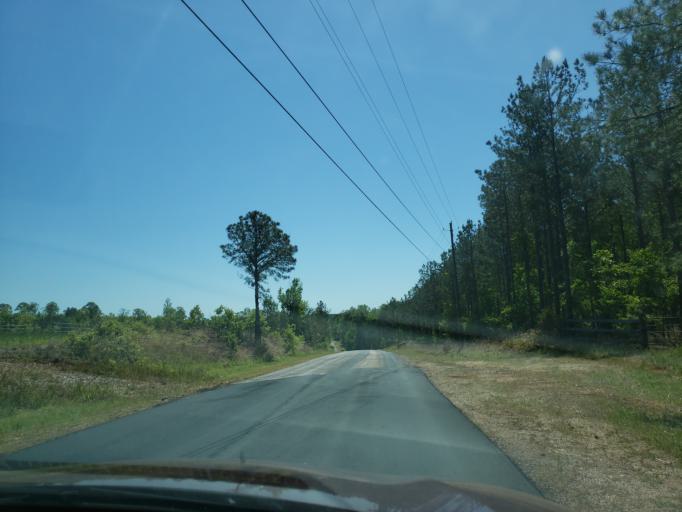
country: US
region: Alabama
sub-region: Tallapoosa County
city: Dadeville
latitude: 32.7012
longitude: -85.8674
